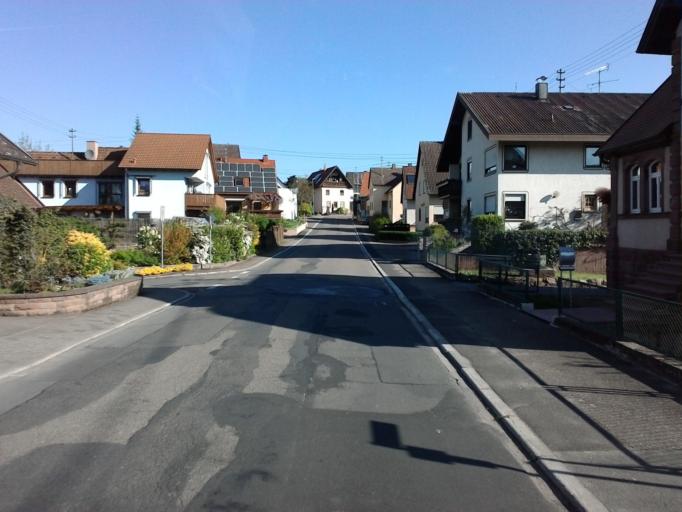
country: DE
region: Bavaria
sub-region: Regierungsbezirk Unterfranken
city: Kreuzwertheim
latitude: 49.7709
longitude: 9.5624
